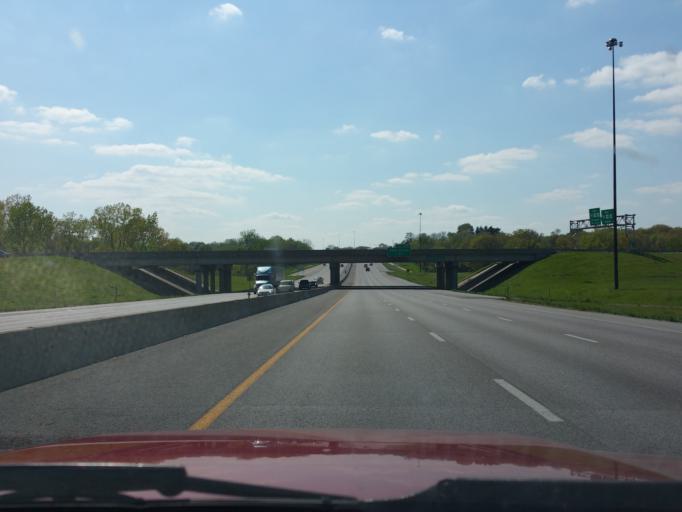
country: US
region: Kansas
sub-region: Johnson County
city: Shawnee
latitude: 39.1062
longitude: -94.7376
